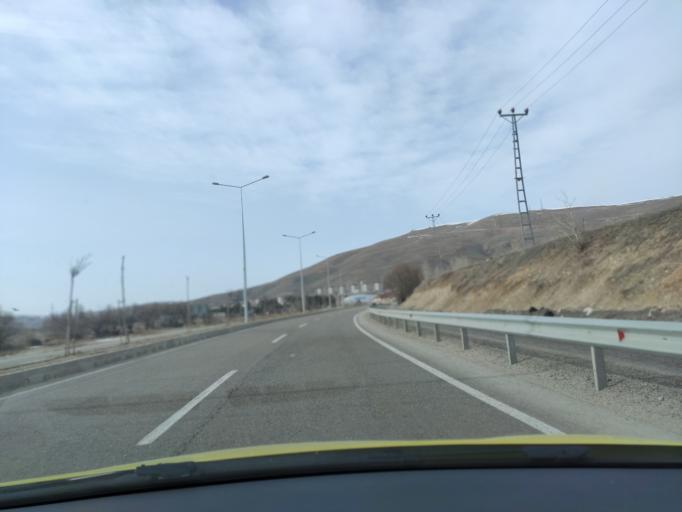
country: TR
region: Bayburt
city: Bayburt
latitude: 40.2285
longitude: 40.2580
